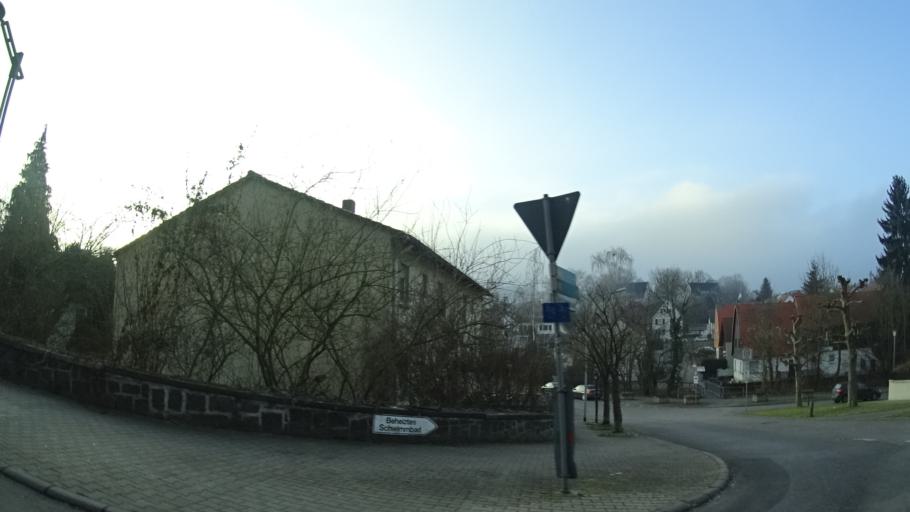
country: DE
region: Hesse
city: Ober-Ramstadt
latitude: 49.8228
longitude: 8.7477
